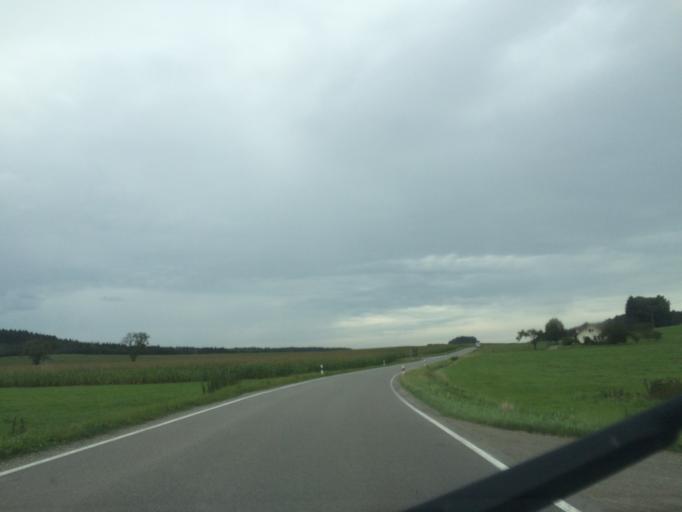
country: DE
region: Baden-Wuerttemberg
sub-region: Tuebingen Region
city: Bad Waldsee
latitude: 47.9431
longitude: 9.7680
